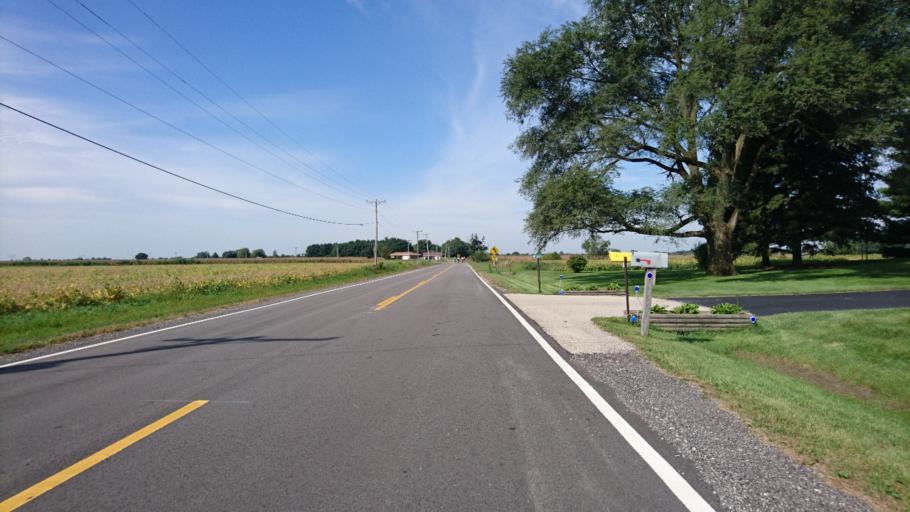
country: US
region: Illinois
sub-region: Will County
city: Elwood
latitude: 41.4081
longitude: -88.0892
